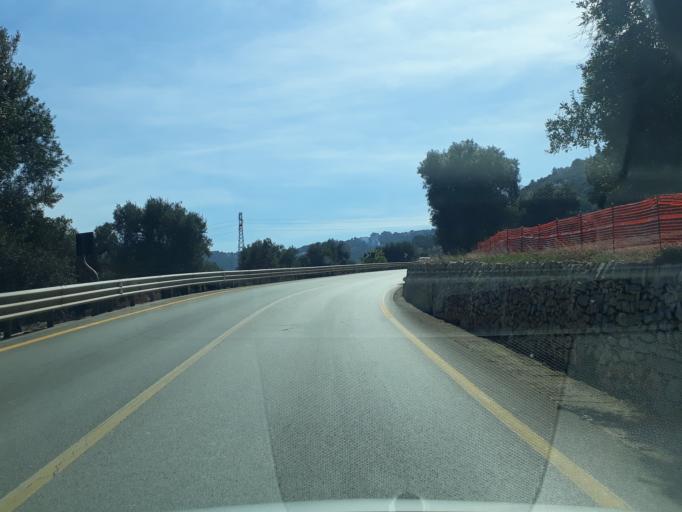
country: IT
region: Apulia
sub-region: Provincia di Brindisi
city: Lamie di Olimpie-Selva
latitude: 40.8190
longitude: 17.3456
